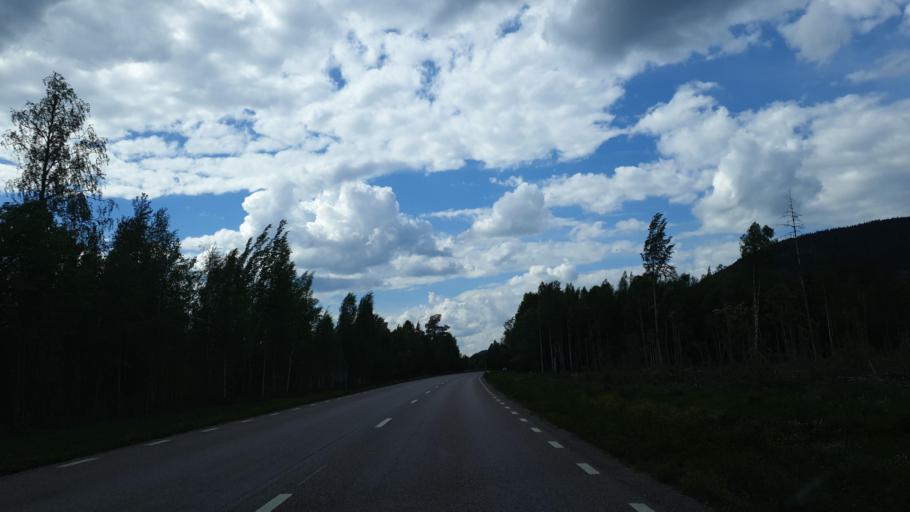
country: SE
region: Norrbotten
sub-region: Alvsbyns Kommun
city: AElvsbyn
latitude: 65.7820
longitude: 20.7743
